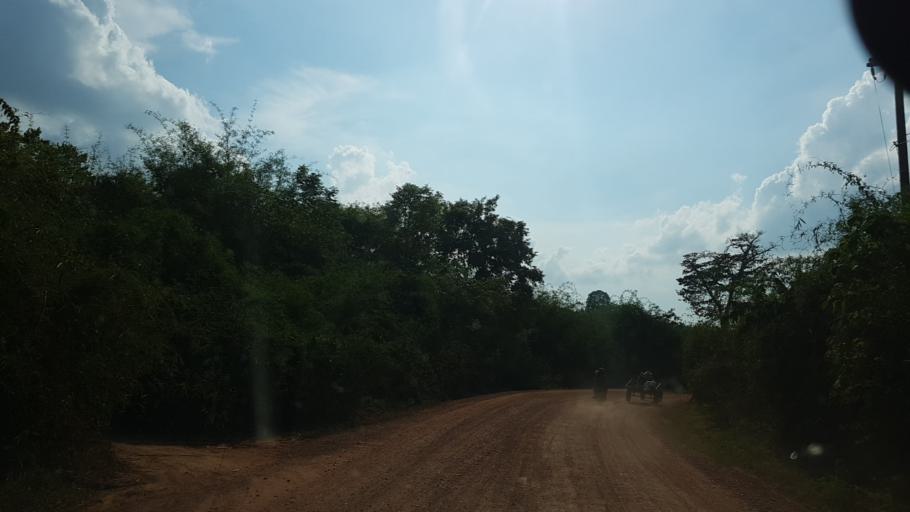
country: LA
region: Vientiane
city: Muang Phon-Hong
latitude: 18.3476
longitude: 102.2840
